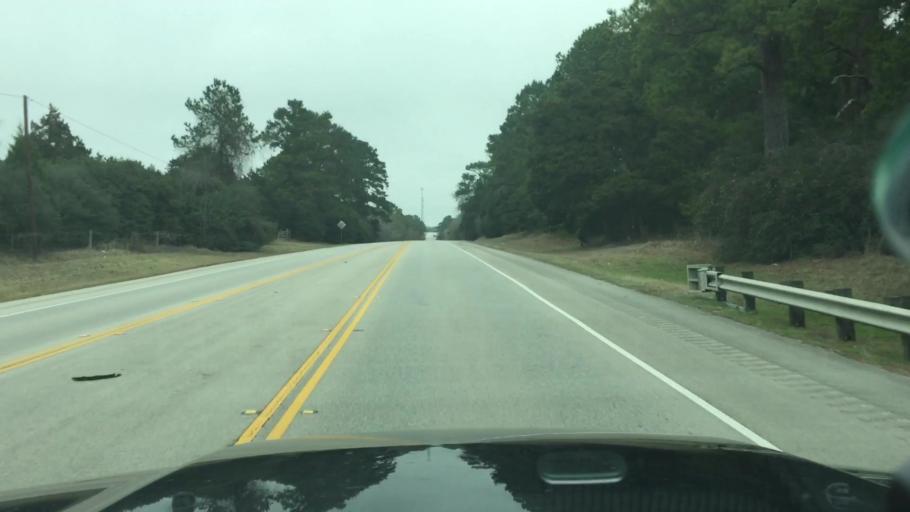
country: US
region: Texas
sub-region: Fayette County
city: La Grange
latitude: 30.0086
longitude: -96.8949
